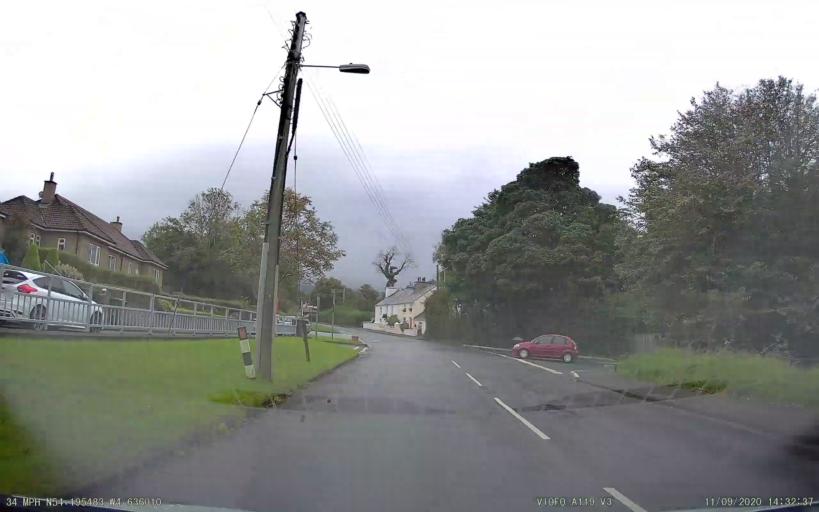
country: IM
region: Castletown
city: Castletown
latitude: 54.1955
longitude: -4.6360
